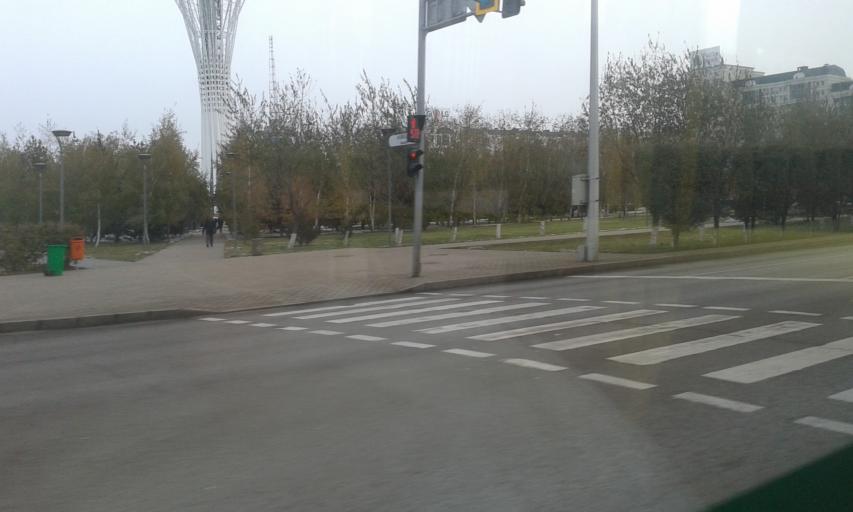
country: KZ
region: Astana Qalasy
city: Astana
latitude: 51.1263
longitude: 71.4278
